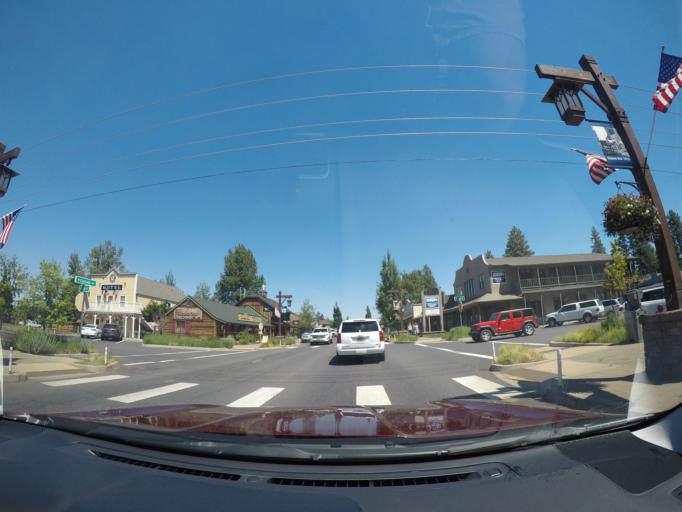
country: US
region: Oregon
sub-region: Deschutes County
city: Sisters
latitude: 44.2913
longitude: -121.5526
